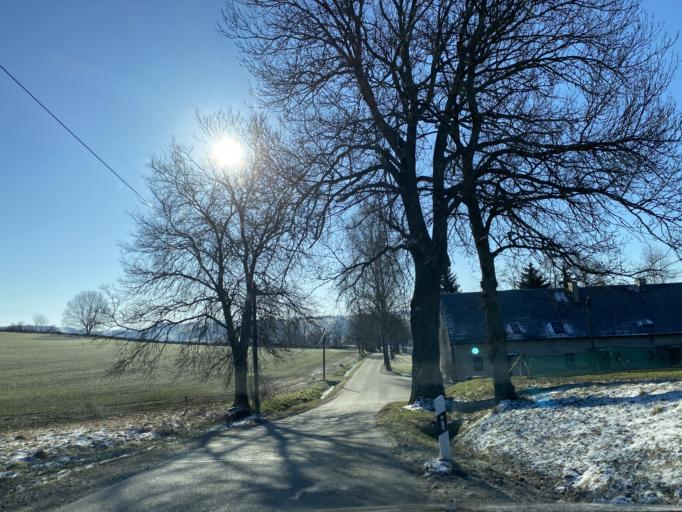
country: DE
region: Saxony
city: Wiesa
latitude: 50.6185
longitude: 13.0058
